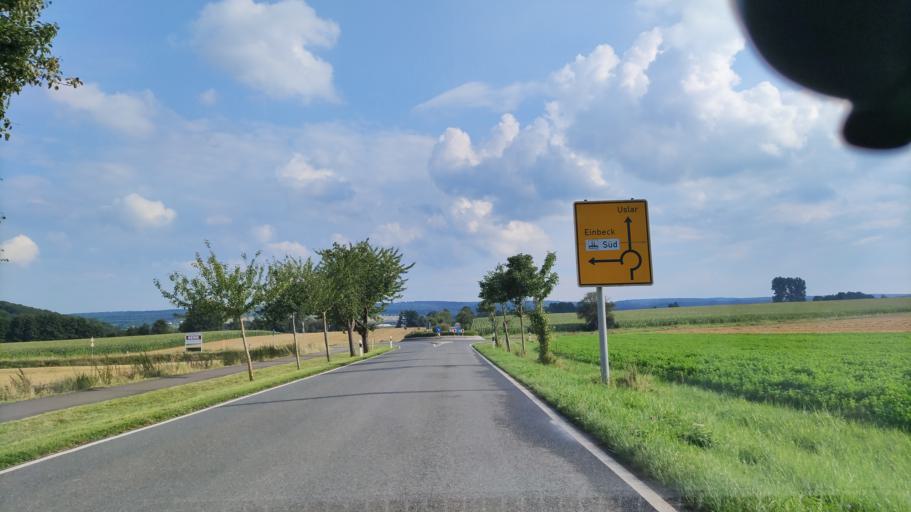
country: DE
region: Lower Saxony
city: Dassel
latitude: 51.7930
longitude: 9.6855
